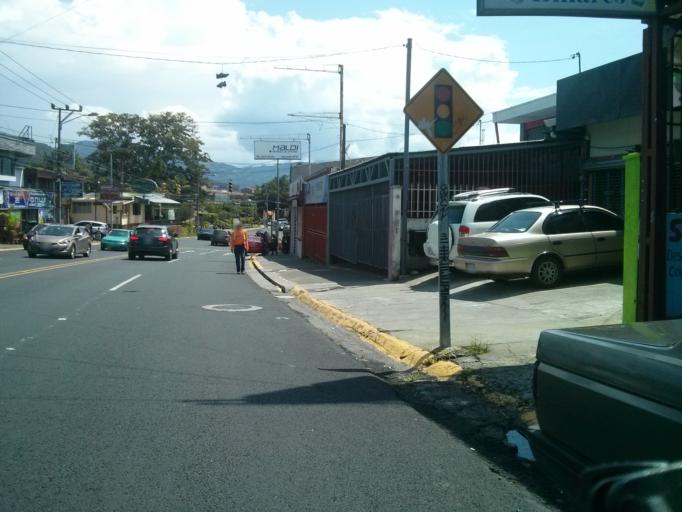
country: CR
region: San Jose
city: San Pedro
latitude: 9.9065
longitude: -84.0568
